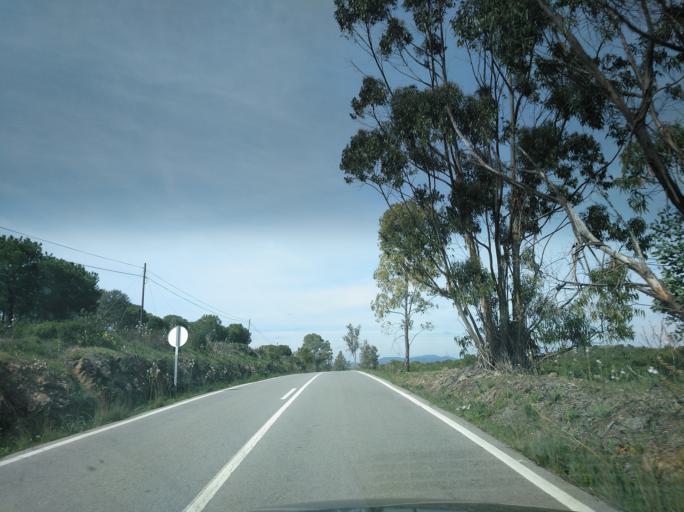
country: PT
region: Beja
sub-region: Mertola
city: Mertola
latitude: 37.5660
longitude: -7.6681
